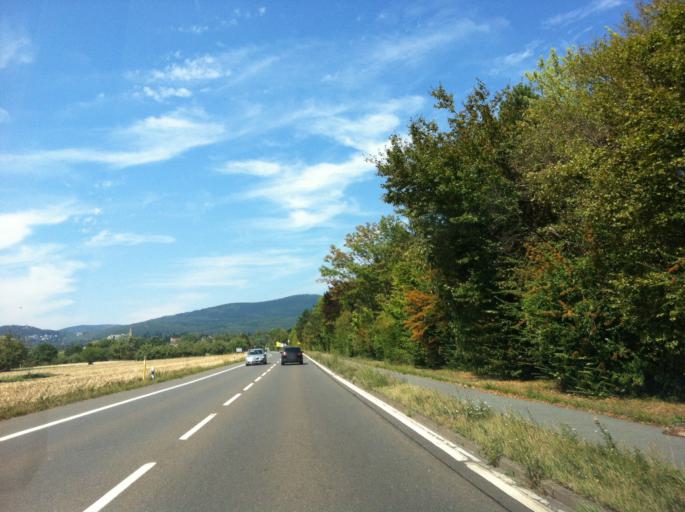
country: DE
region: Hesse
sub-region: Regierungsbezirk Darmstadt
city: Kronberg
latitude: 50.1690
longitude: 8.5304
